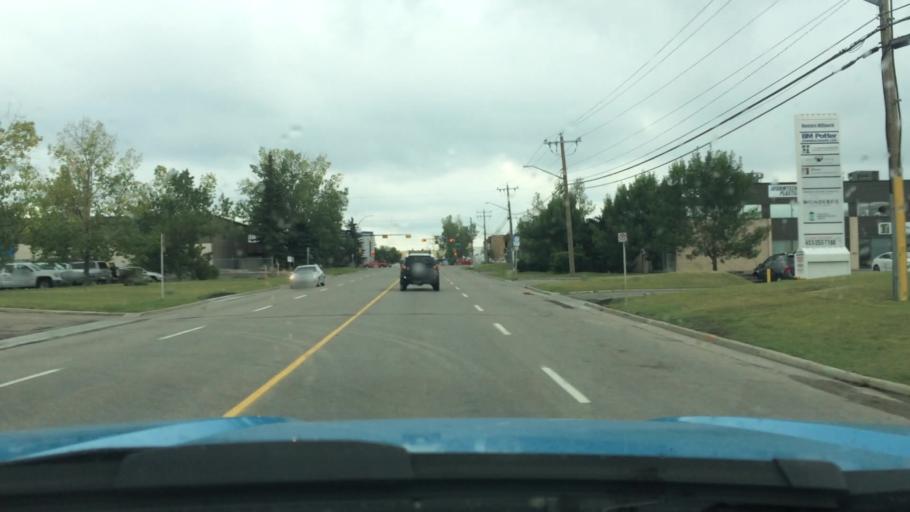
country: CA
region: Alberta
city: Calgary
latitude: 51.0785
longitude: -114.0117
